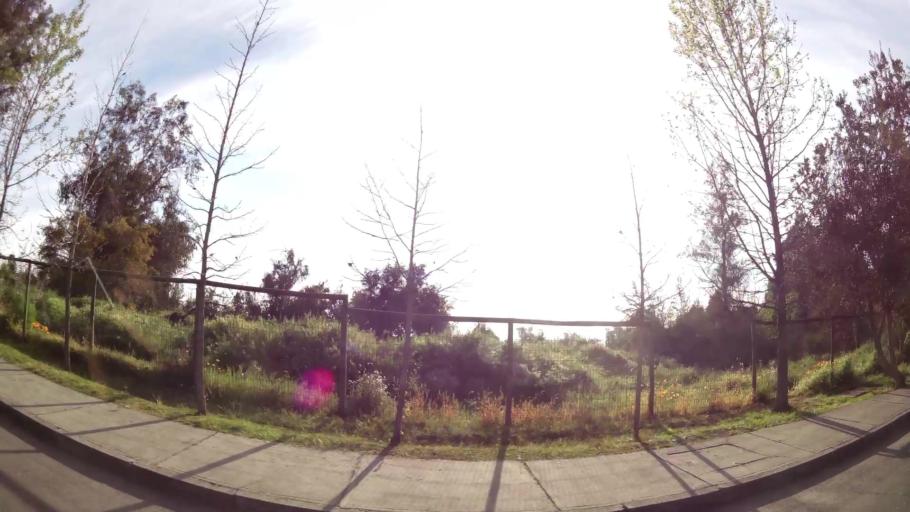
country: CL
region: Santiago Metropolitan
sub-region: Provincia de Santiago
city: Villa Presidente Frei, Nunoa, Santiago, Chile
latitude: -33.5014
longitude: -70.5481
